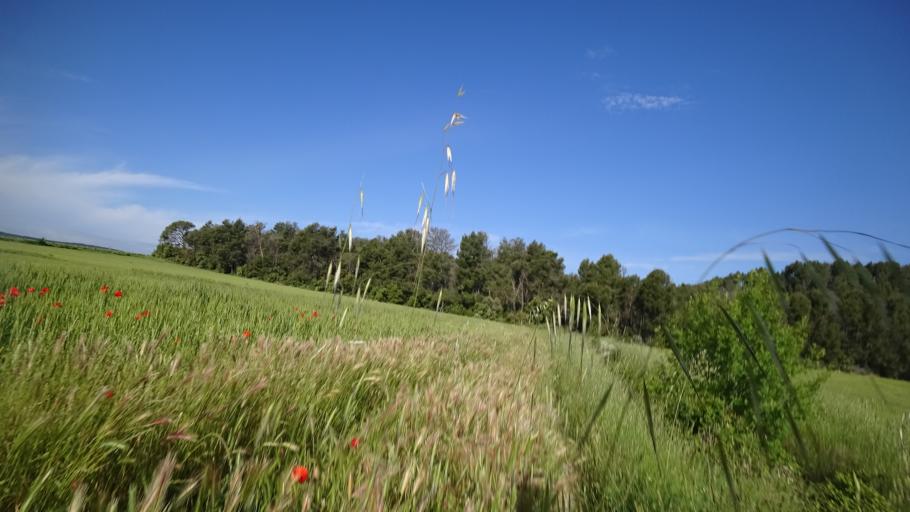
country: FR
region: Languedoc-Roussillon
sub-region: Departement de l'Aude
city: Lezignan-Corbieres
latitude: 43.2363
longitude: 2.7508
